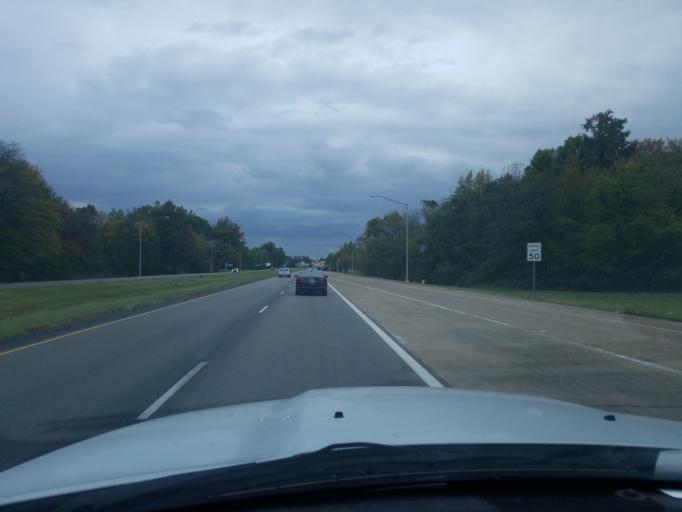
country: US
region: Indiana
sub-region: Vanderburgh County
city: Evansville
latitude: 37.9448
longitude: -87.5430
